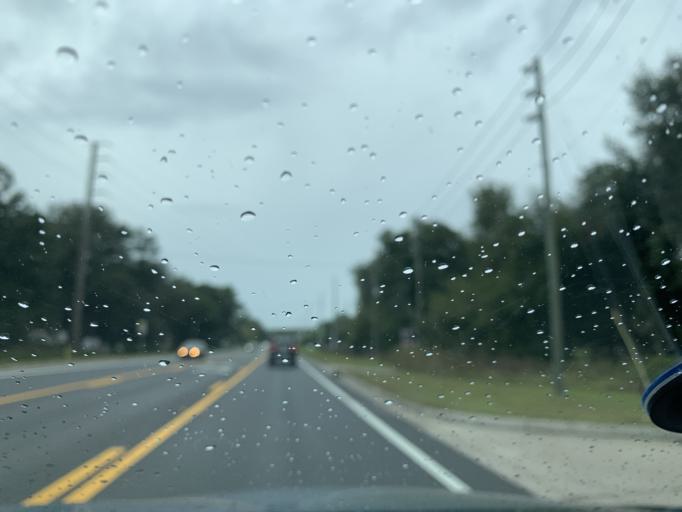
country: US
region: Florida
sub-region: Pasco County
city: Zephyrhills
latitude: 28.2519
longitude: -82.1928
